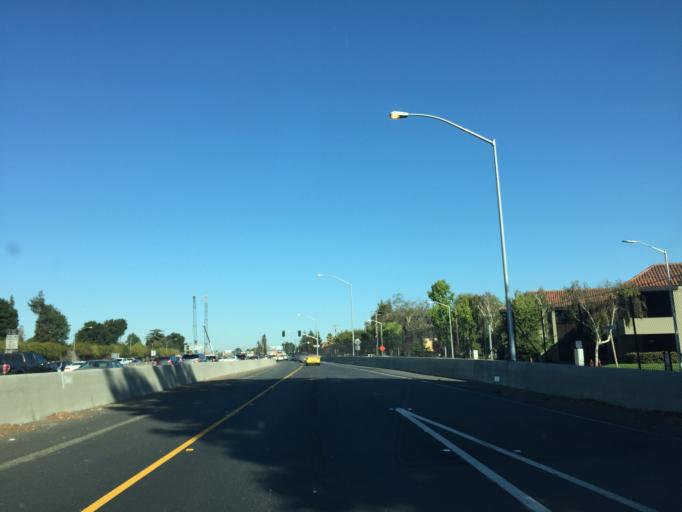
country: US
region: California
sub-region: Santa Clara County
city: Palo Alto
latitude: 37.4501
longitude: -122.1239
